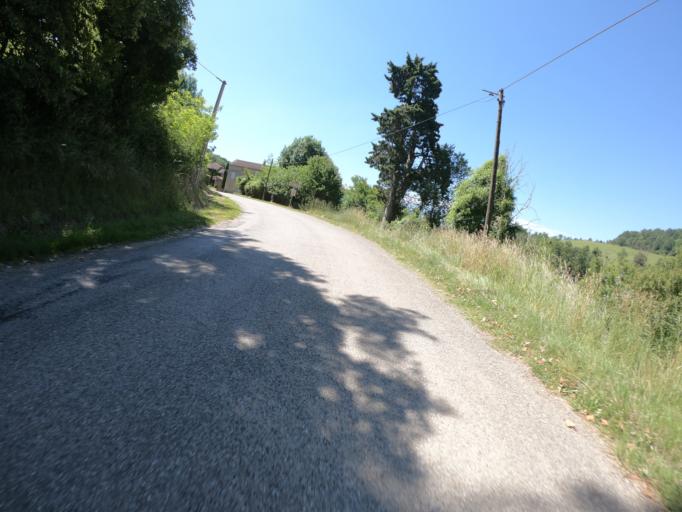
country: FR
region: Midi-Pyrenees
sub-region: Departement de l'Ariege
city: Mirepoix
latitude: 43.0943
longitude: 1.7784
